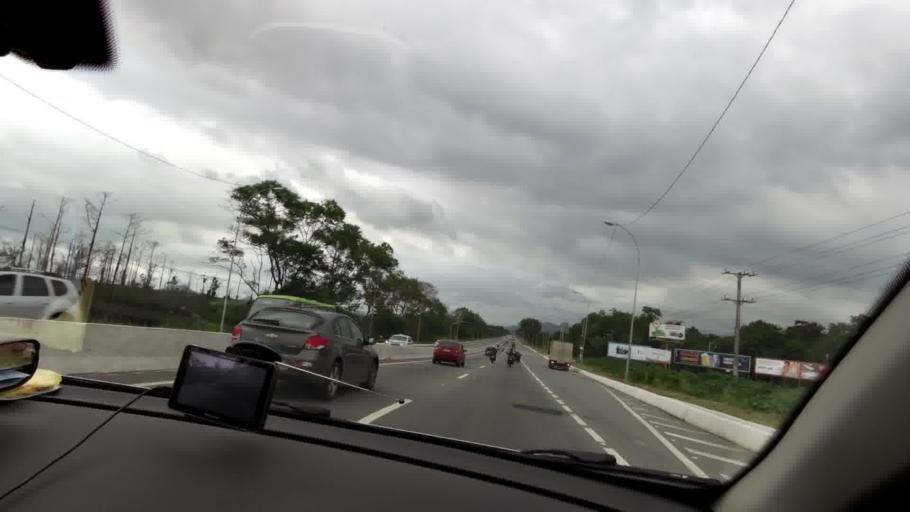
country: BR
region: Espirito Santo
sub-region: Vila Velha
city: Vila Velha
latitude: -20.2400
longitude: -40.2796
